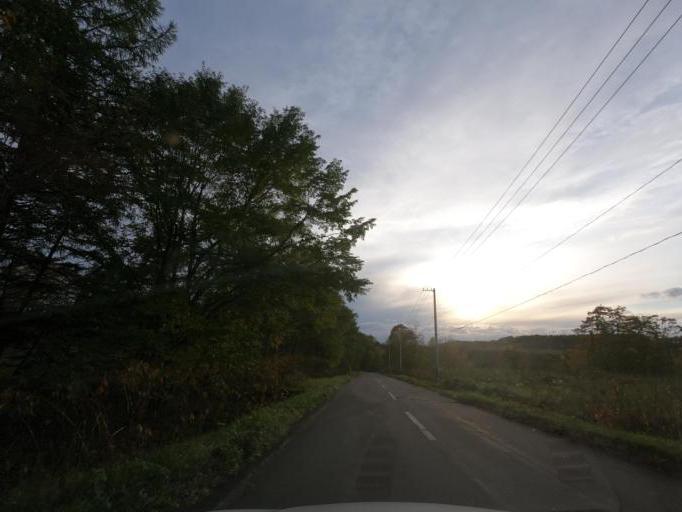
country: JP
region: Hokkaido
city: Obihiro
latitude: 42.5462
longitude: 143.4025
